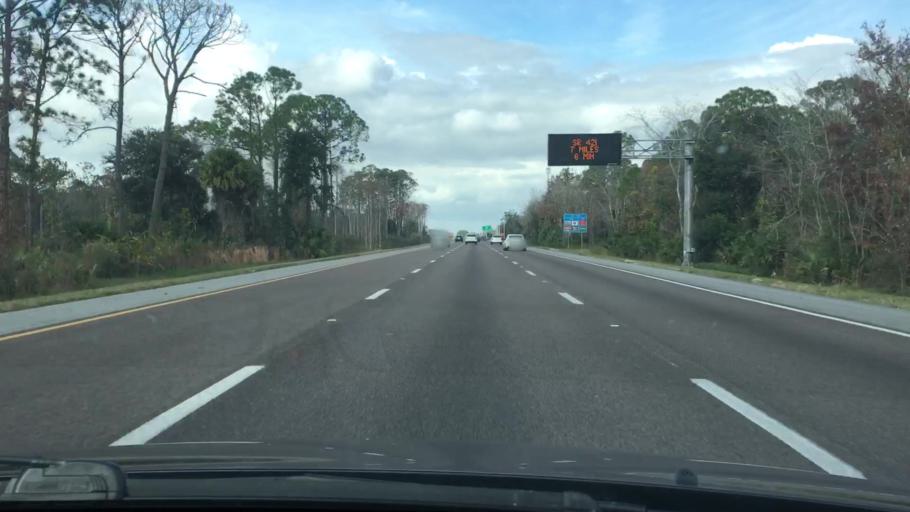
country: US
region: Florida
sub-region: Volusia County
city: Glencoe
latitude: 29.0044
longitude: -80.9822
